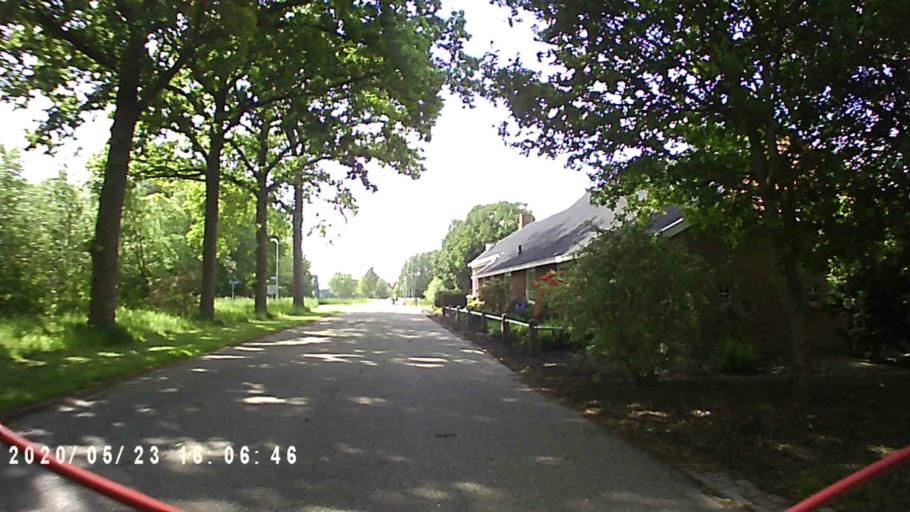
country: NL
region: Groningen
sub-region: Gemeente Appingedam
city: Appingedam
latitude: 53.2467
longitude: 6.8911
